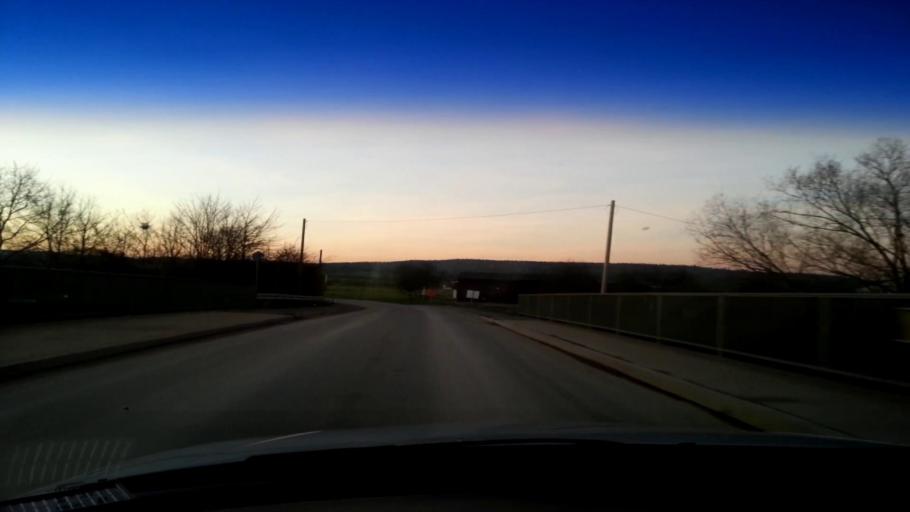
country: DE
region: Bavaria
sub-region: Upper Franconia
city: Zapfendorf
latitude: 50.0220
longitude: 10.9303
